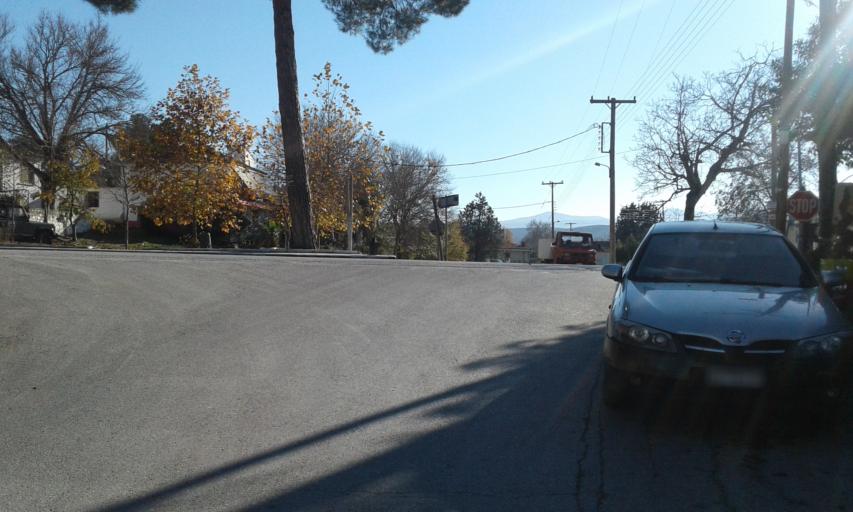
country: GR
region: Central Macedonia
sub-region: Nomos Thessalonikis
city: Gerakarou
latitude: 40.6355
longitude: 23.2452
